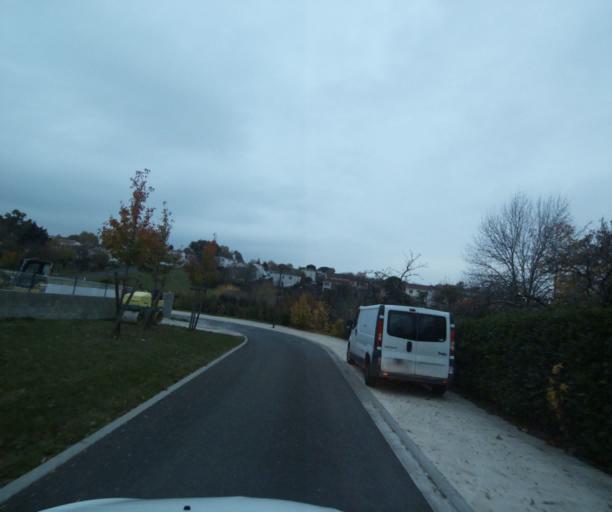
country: FR
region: Poitou-Charentes
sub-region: Departement de la Charente-Maritime
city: Saintes
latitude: 45.7451
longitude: -0.6088
